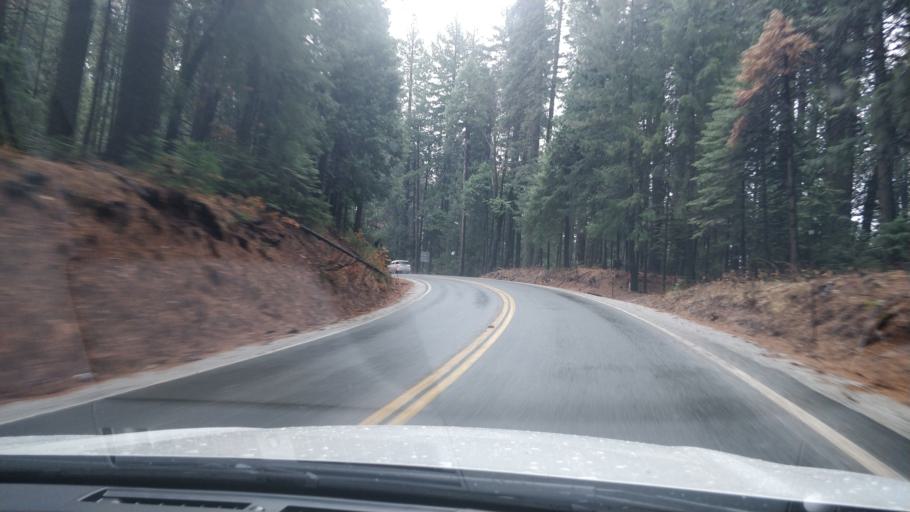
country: US
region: California
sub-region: Nevada County
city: Nevada City
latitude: 39.3221
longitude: -120.8312
